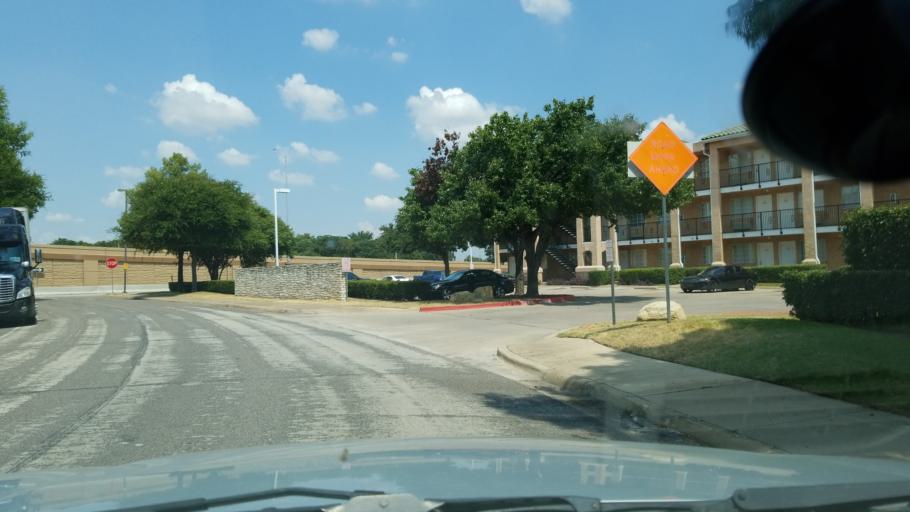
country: US
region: Texas
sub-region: Dallas County
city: Irving
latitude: 32.8599
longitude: -96.9009
